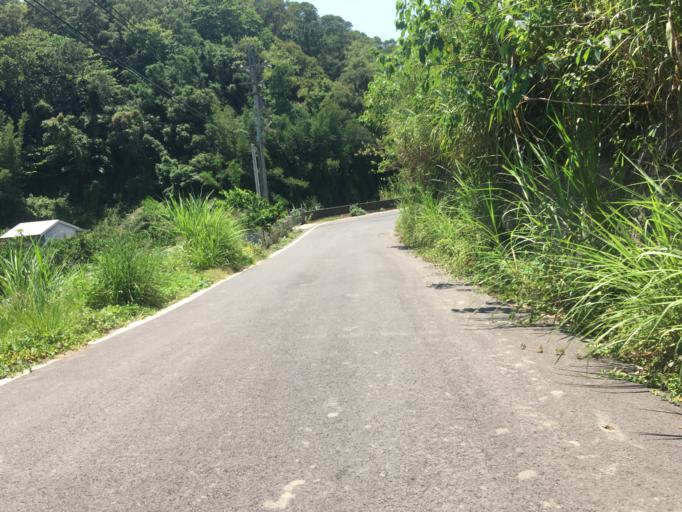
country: TW
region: Taiwan
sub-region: Hsinchu
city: Hsinchu
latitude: 24.7301
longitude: 120.9835
